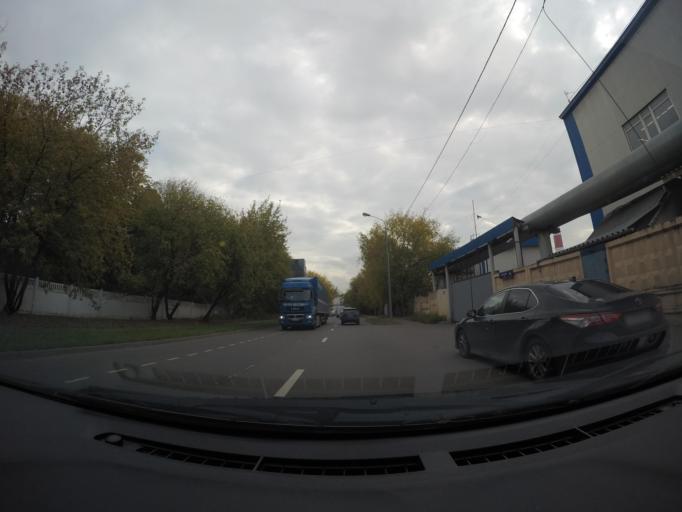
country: RU
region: Moscow
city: Lefortovo
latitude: 55.7579
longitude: 37.7345
